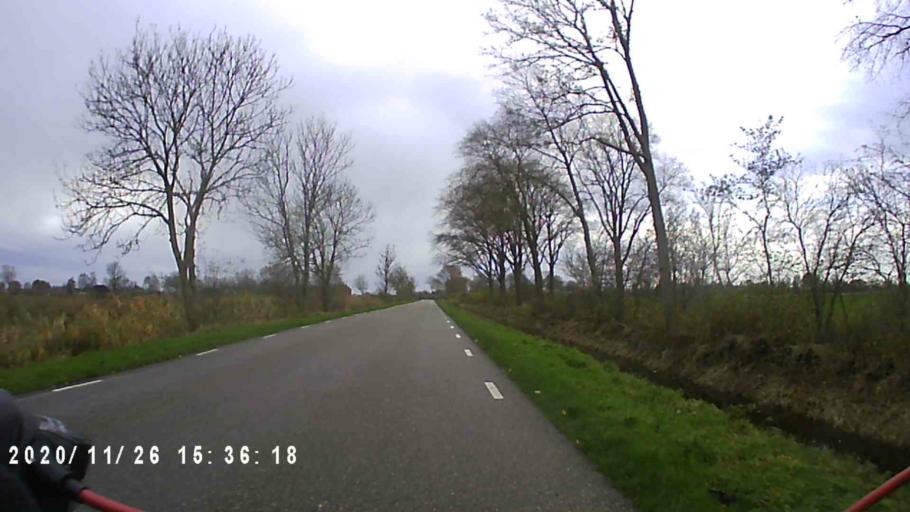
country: NL
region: Groningen
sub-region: Gemeente Slochteren
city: Slochteren
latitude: 53.3039
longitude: 6.7364
